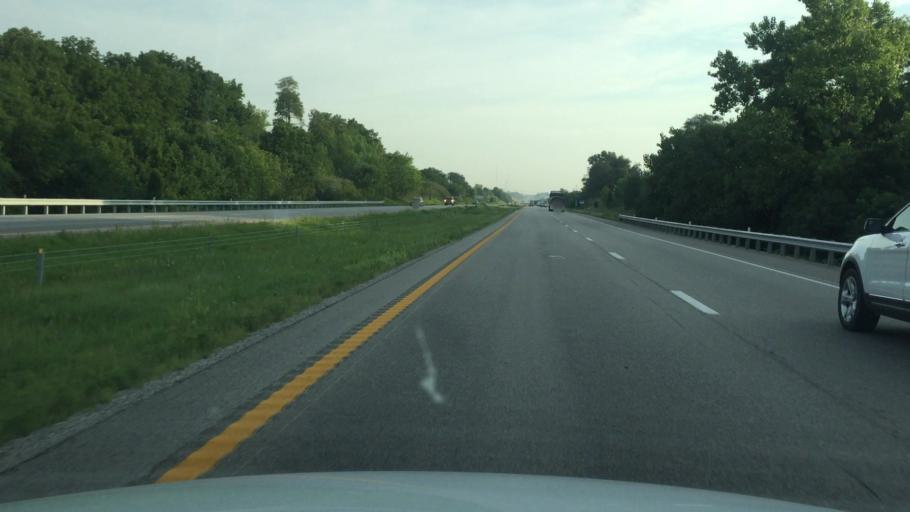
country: US
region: Missouri
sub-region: Buchanan County
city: Saint Joseph
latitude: 39.6918
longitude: -94.7882
